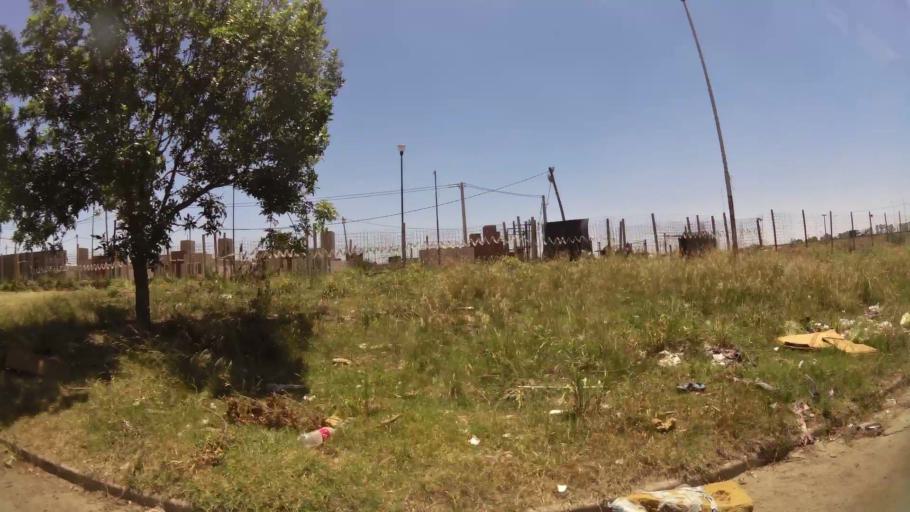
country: AR
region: Cordoba
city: Malvinas Argentinas
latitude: -31.3785
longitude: -64.1289
